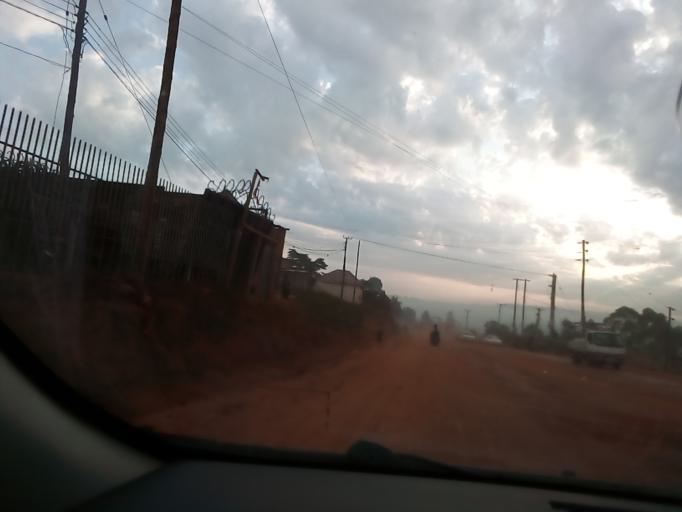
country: UG
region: Central Region
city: Masaka
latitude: -0.3321
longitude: 31.7449
